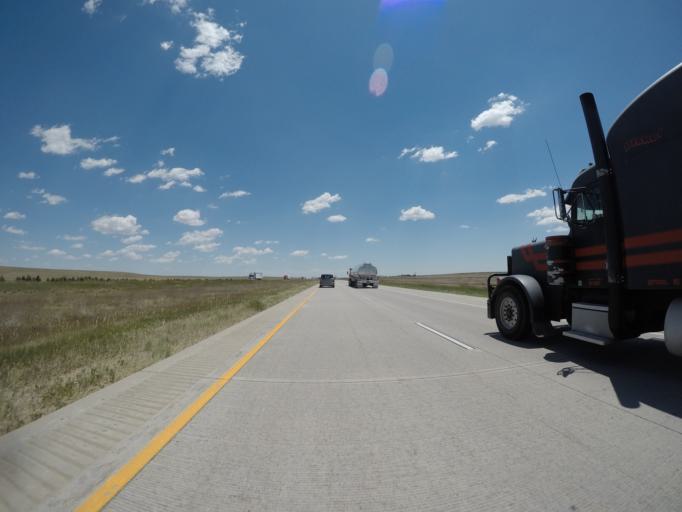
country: US
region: Colorado
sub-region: Lincoln County
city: Limon
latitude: 39.2790
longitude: -103.7614
